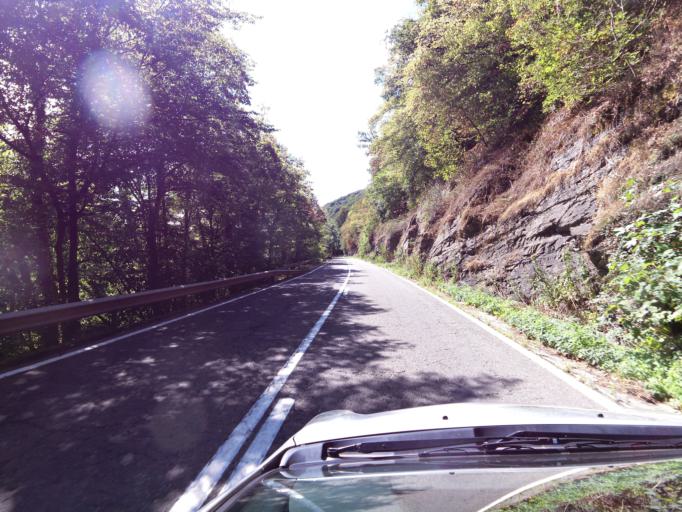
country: BE
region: Wallonia
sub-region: Province du Luxembourg
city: Rendeux
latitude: 50.2220
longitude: 5.5212
